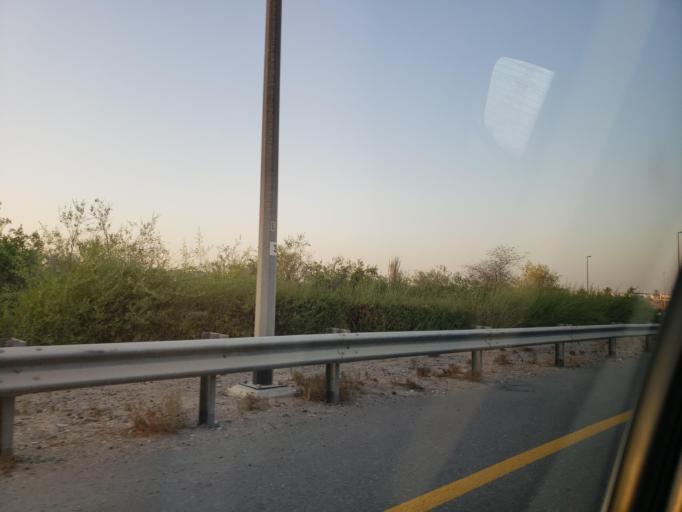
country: AE
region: Dubai
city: Dubai
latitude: 25.0011
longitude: 55.2571
